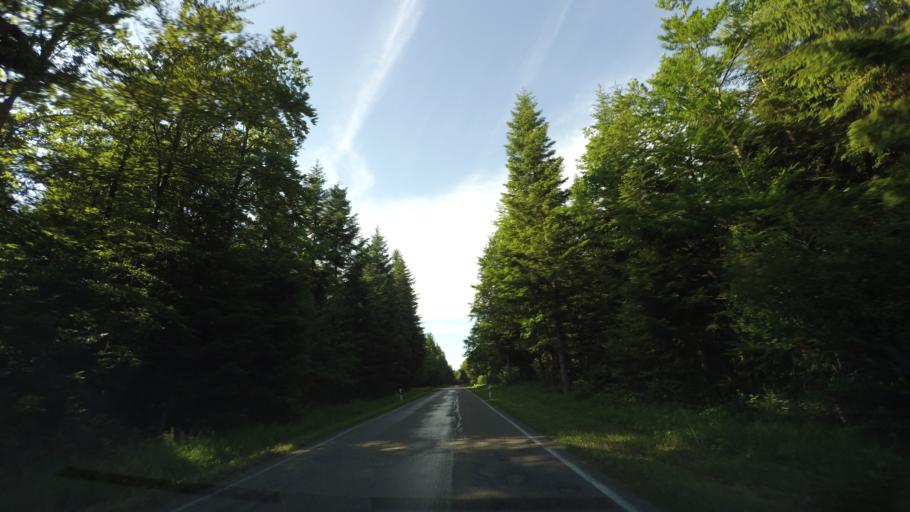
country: DE
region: Baden-Wuerttemberg
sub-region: Regierungsbezirk Stuttgart
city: Fichtenberg
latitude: 48.9637
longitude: 9.6785
